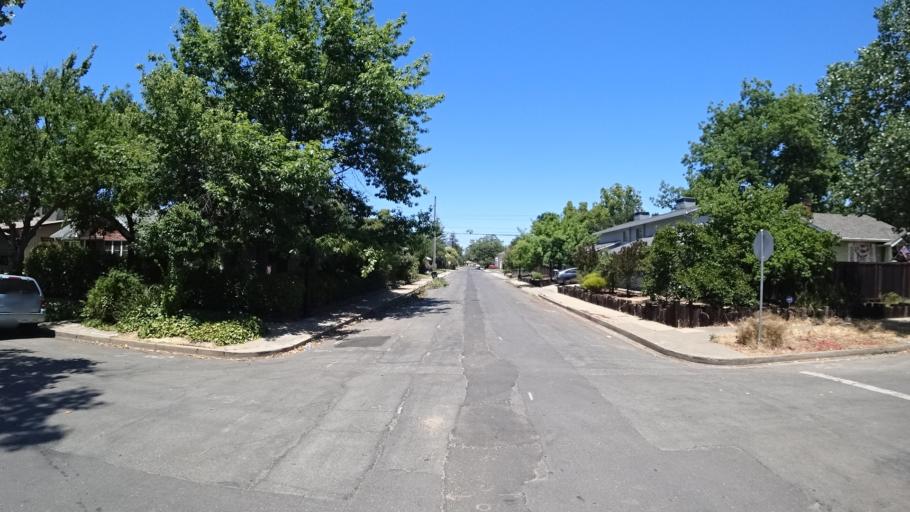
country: US
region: California
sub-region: Sacramento County
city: Parkway
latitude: 38.5409
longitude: -121.4479
